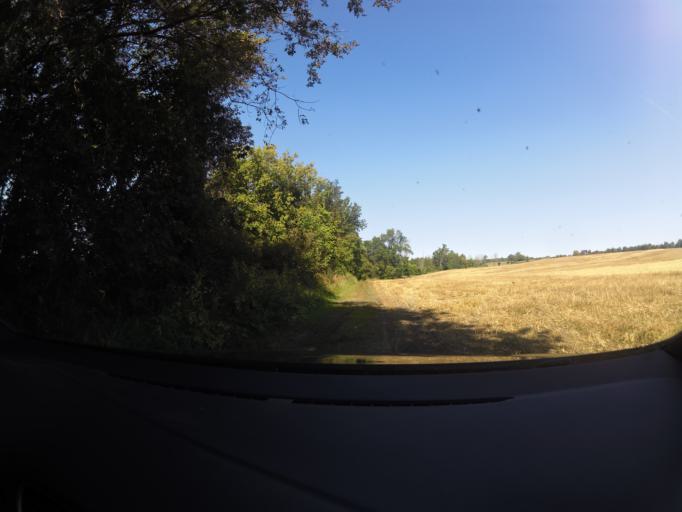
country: CA
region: Ontario
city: Arnprior
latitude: 45.3609
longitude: -76.2683
